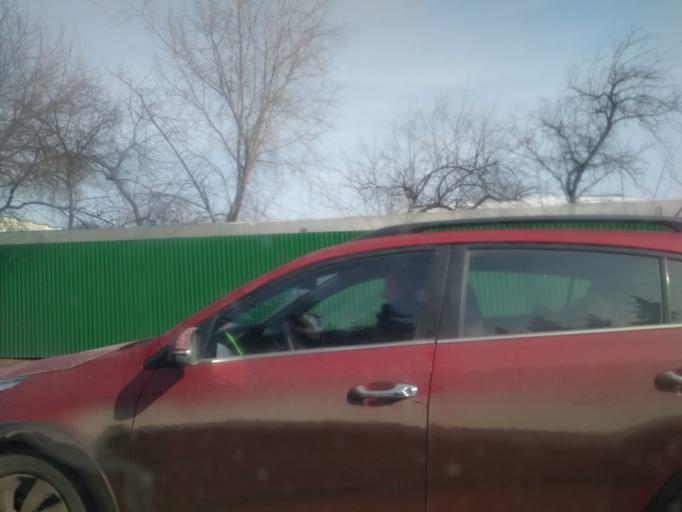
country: RU
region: Moskovskaya
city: Zhukovskiy
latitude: 55.5943
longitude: 38.1144
